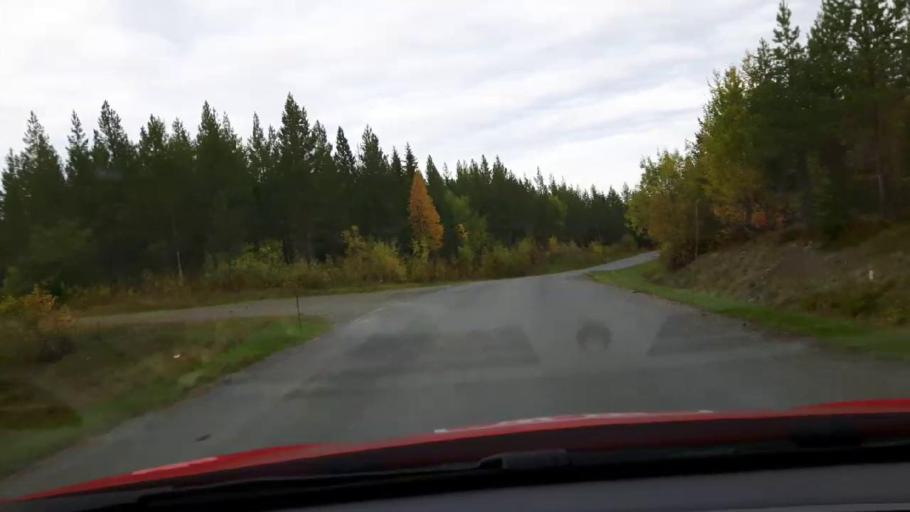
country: SE
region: Jaemtland
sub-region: Krokoms Kommun
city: Krokom
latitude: 63.2161
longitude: 14.1201
